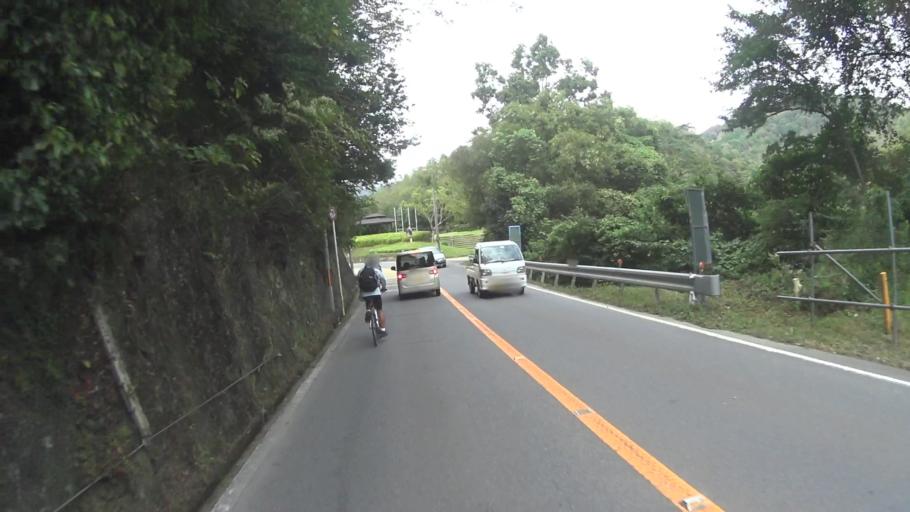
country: JP
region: Kyoto
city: Uji
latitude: 34.8809
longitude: 135.8239
